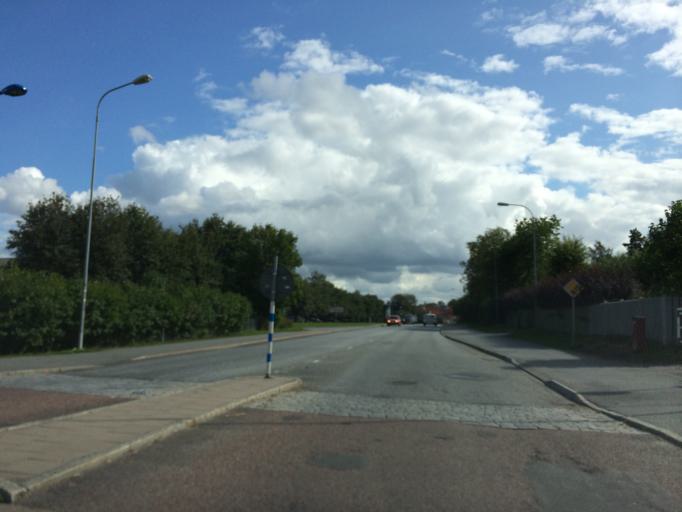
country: SE
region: Stockholm
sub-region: Sollentuna Kommun
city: Sollentuna
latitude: 59.4294
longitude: 17.9347
